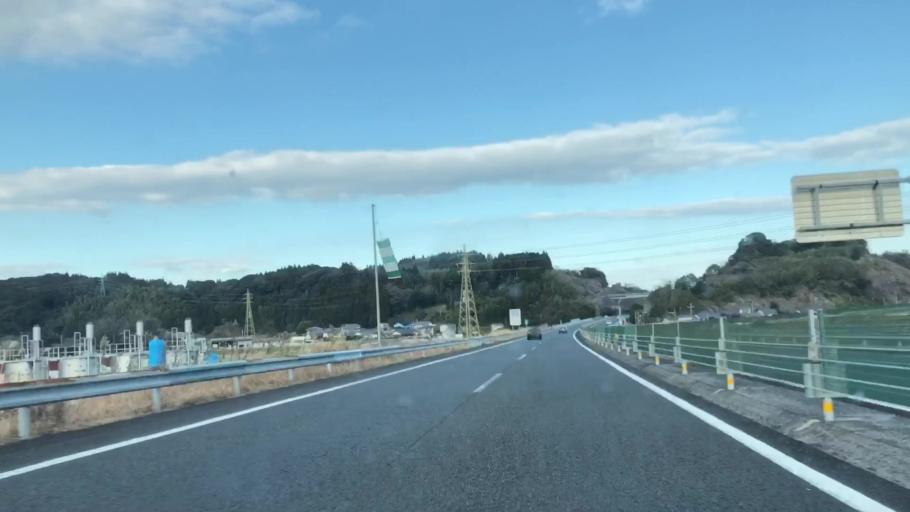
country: JP
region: Miyazaki
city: Miyazaki-shi
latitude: 31.8609
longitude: 131.3795
